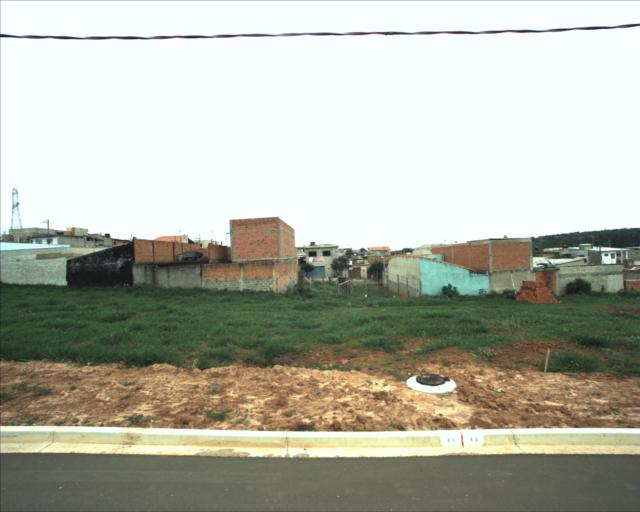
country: BR
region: Sao Paulo
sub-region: Sorocaba
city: Sorocaba
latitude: -23.4178
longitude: -47.4302
